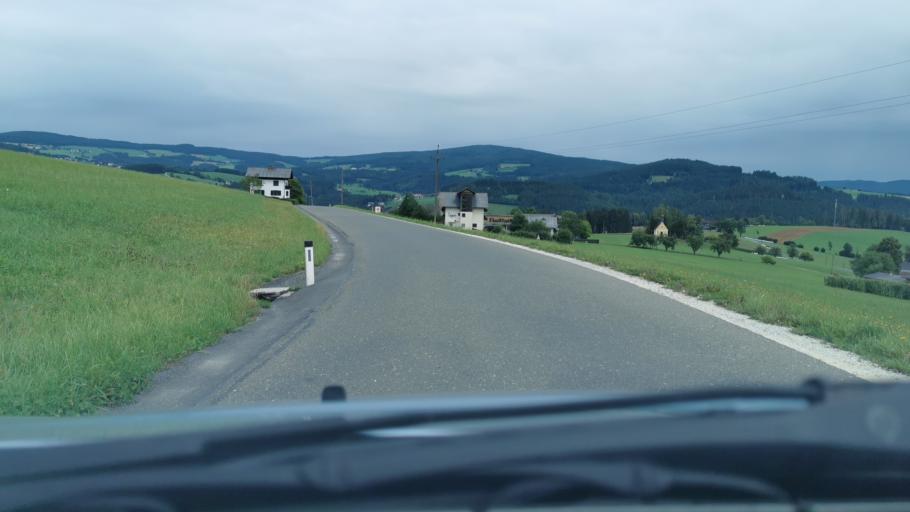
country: AT
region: Styria
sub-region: Politischer Bezirk Weiz
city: Strallegg
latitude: 47.3943
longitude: 15.6792
